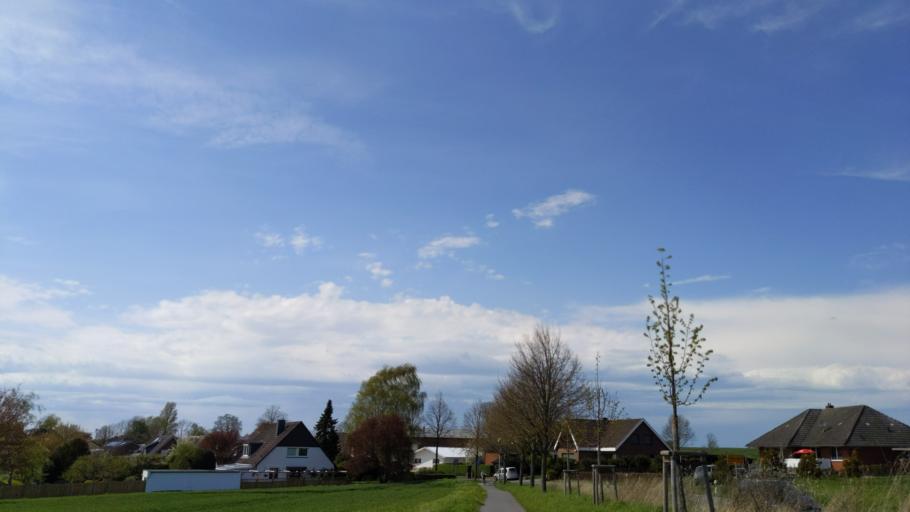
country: DE
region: Schleswig-Holstein
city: Stockelsdorf
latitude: 53.9287
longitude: 10.6435
